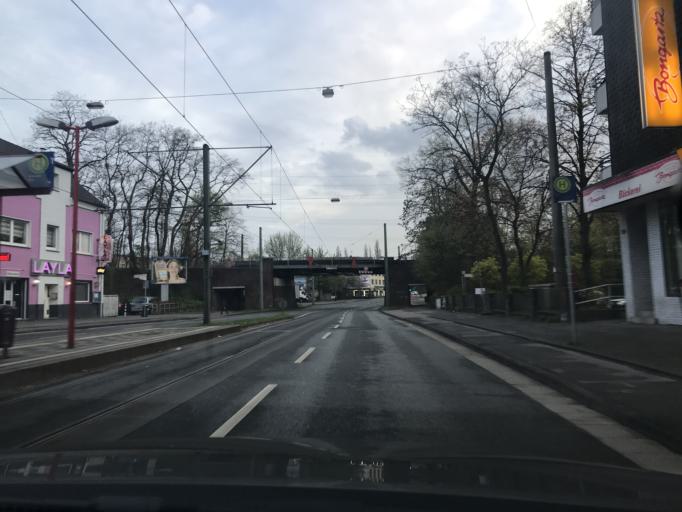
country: DE
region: North Rhine-Westphalia
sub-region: Regierungsbezirk Dusseldorf
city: Dinslaken
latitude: 51.5232
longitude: 6.7429
